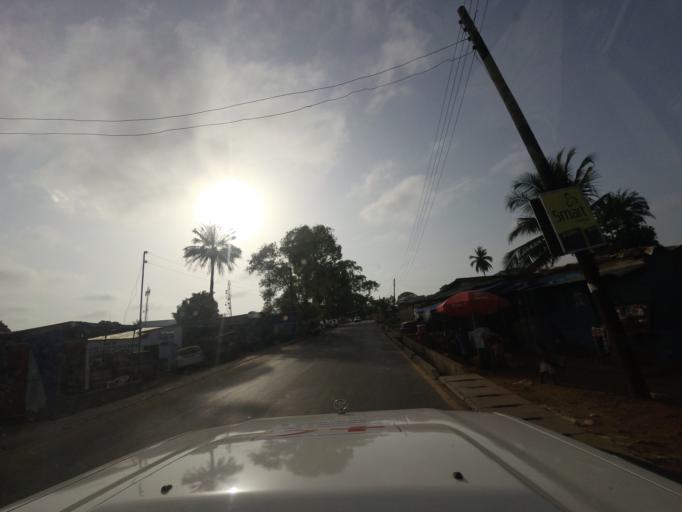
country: SL
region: Western Area
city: Freetown
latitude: 8.4926
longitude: -13.2858
